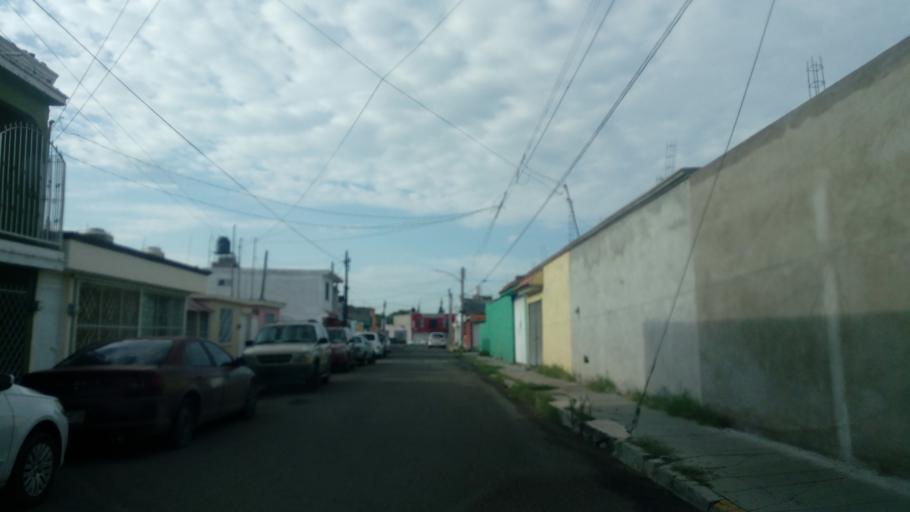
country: MX
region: Durango
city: Victoria de Durango
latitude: 24.0176
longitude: -104.6481
